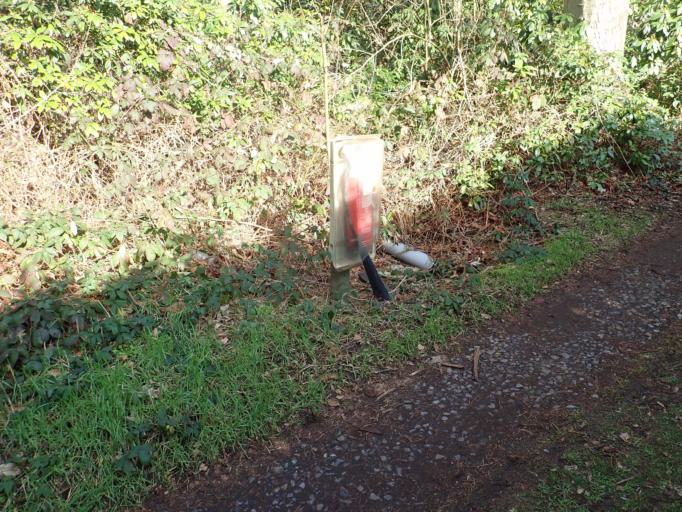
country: BE
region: Flanders
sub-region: Provincie Antwerpen
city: Stabroek
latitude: 51.3576
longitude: 4.3550
